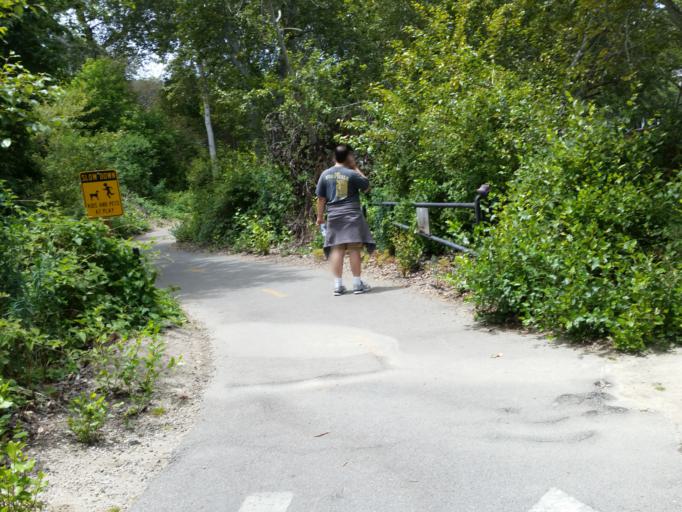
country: US
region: California
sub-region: San Luis Obispo County
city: Avila Beach
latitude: 35.1888
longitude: -120.7193
